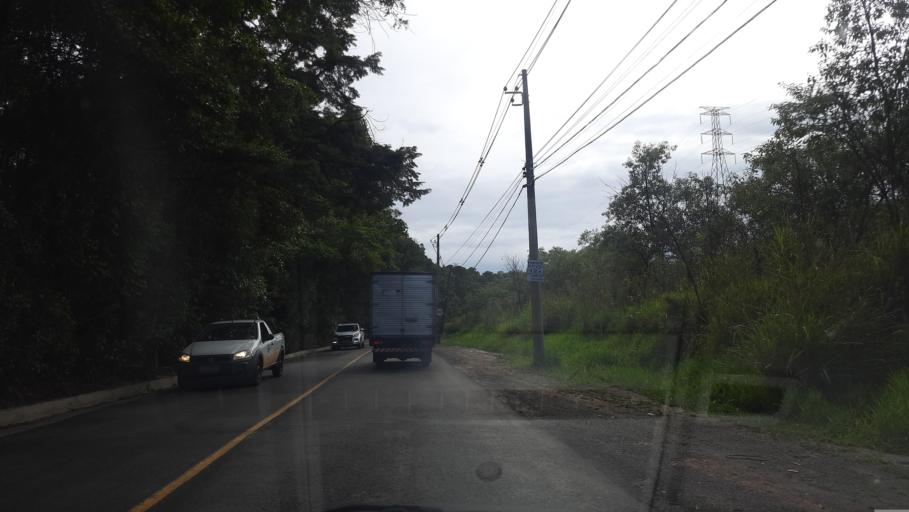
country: BR
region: Sao Paulo
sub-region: Caieiras
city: Caieiras
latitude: -23.3728
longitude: -46.6919
